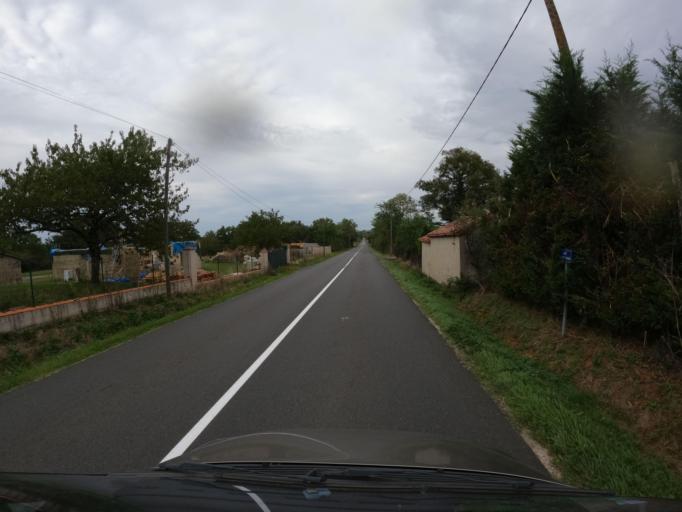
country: FR
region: Poitou-Charentes
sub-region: Departement de la Vienne
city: Saulge
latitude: 46.3507
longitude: 0.8316
